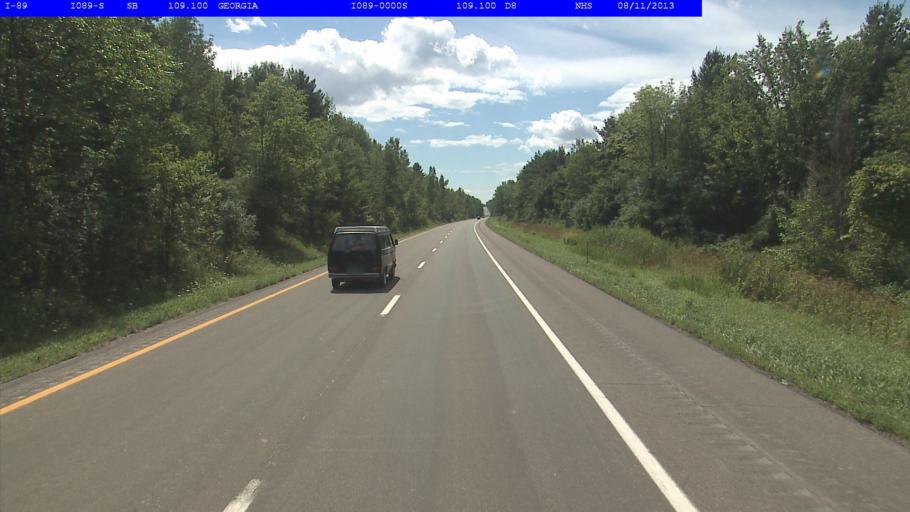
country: US
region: Vermont
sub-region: Franklin County
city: Saint Albans
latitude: 44.7284
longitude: -73.0814
